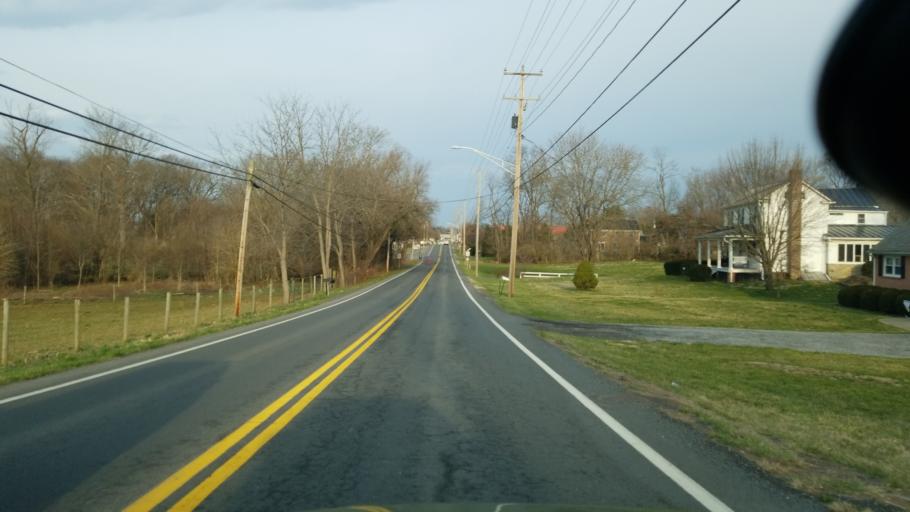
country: US
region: Virginia
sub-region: Clarke County
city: Berryville
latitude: 39.1462
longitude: -77.9665
